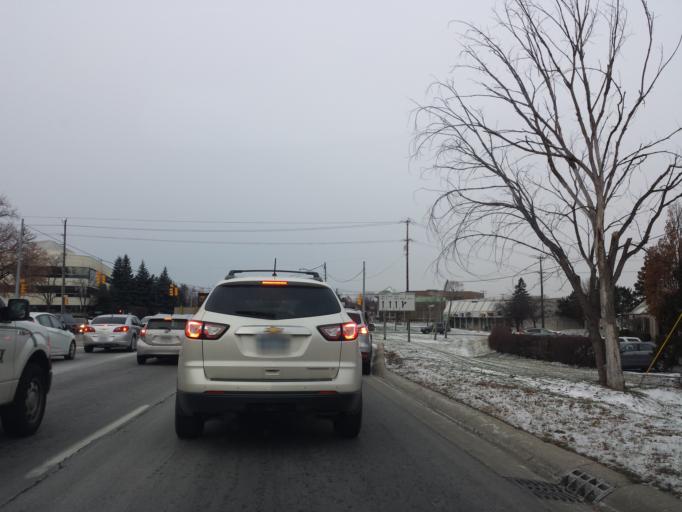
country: US
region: Michigan
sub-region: Oakland County
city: Pontiac
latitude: 42.6032
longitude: -83.2863
